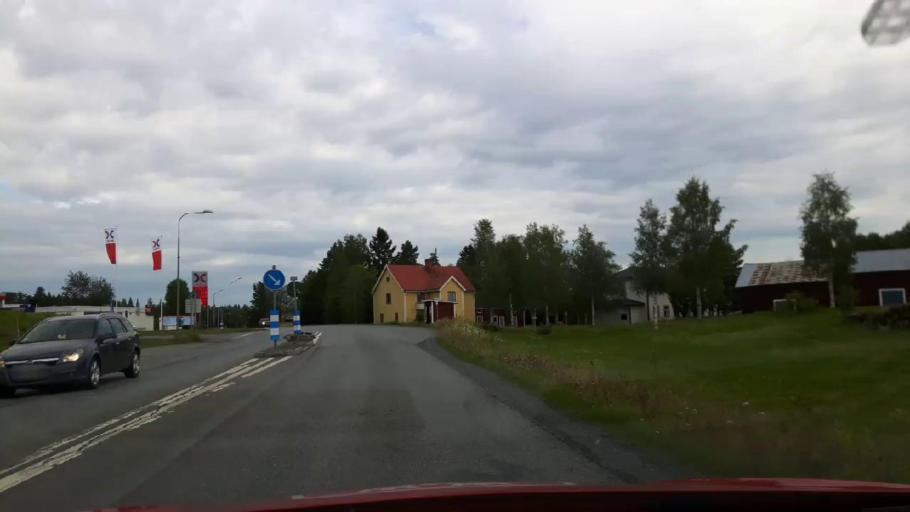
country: SE
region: Jaemtland
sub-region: Stroemsunds Kommun
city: Stroemsund
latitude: 63.5913
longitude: 15.3551
